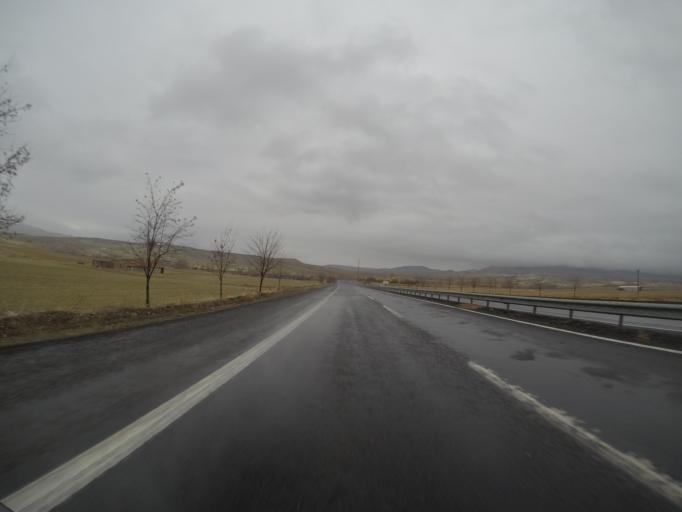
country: TR
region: Nevsehir
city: Avanos
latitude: 38.7115
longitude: 34.9043
